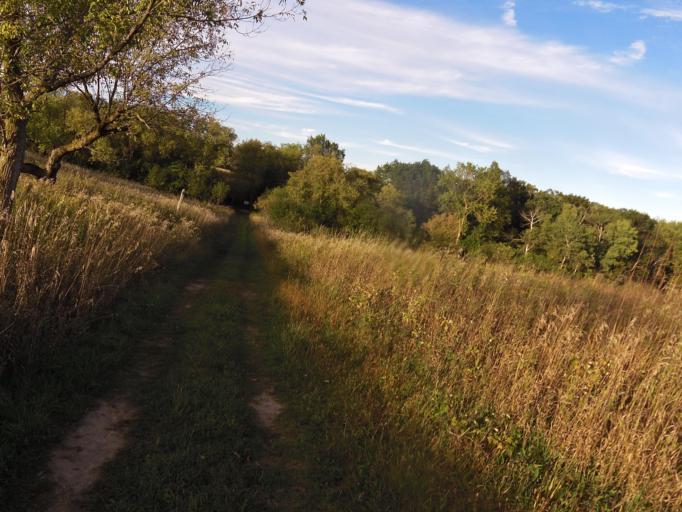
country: US
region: Minnesota
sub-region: Washington County
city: Afton
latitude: 44.8605
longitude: -92.7852
